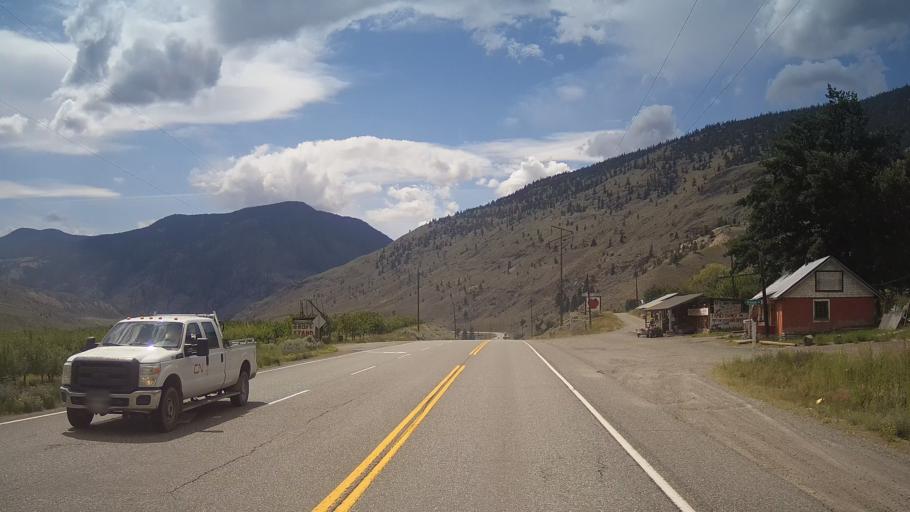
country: CA
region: British Columbia
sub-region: Thompson-Nicola Regional District
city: Ashcroft
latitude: 50.4575
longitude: -121.3044
